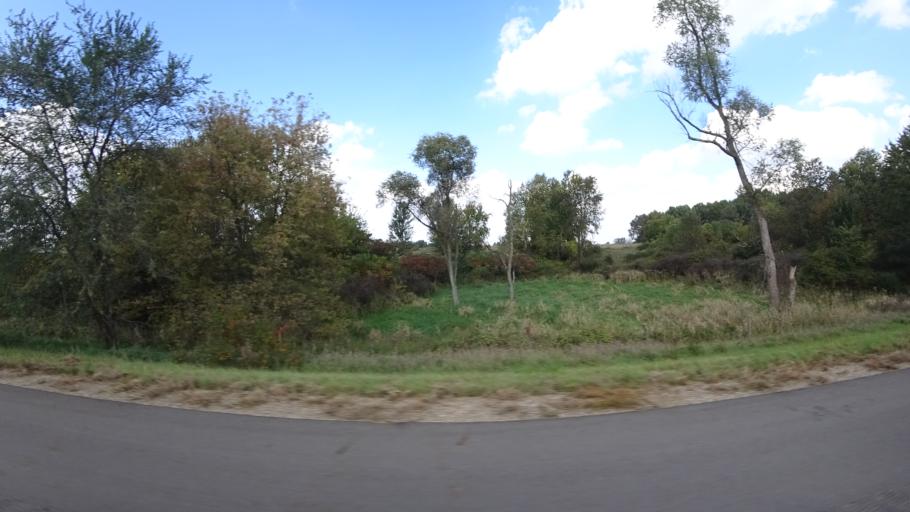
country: US
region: Michigan
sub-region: Branch County
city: Union City
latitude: 42.0686
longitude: -85.1669
